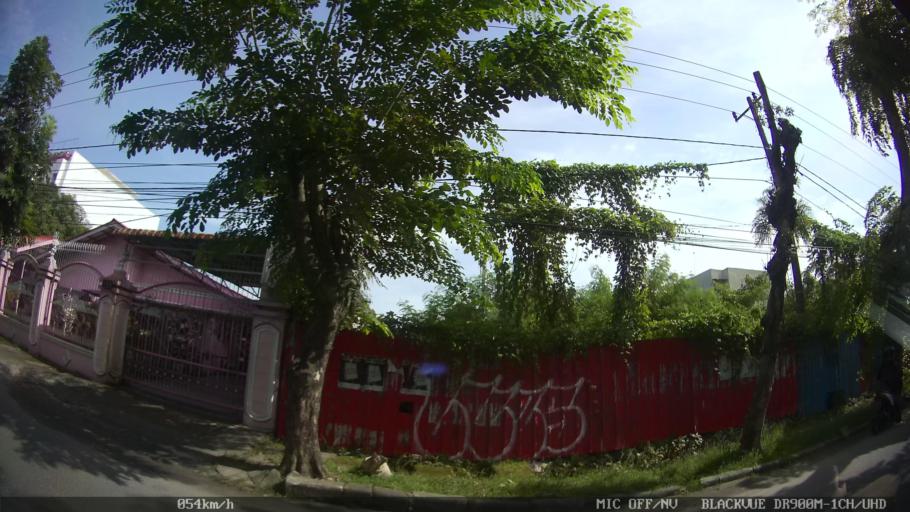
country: ID
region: North Sumatra
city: Medan
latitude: 3.5677
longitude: 98.6450
